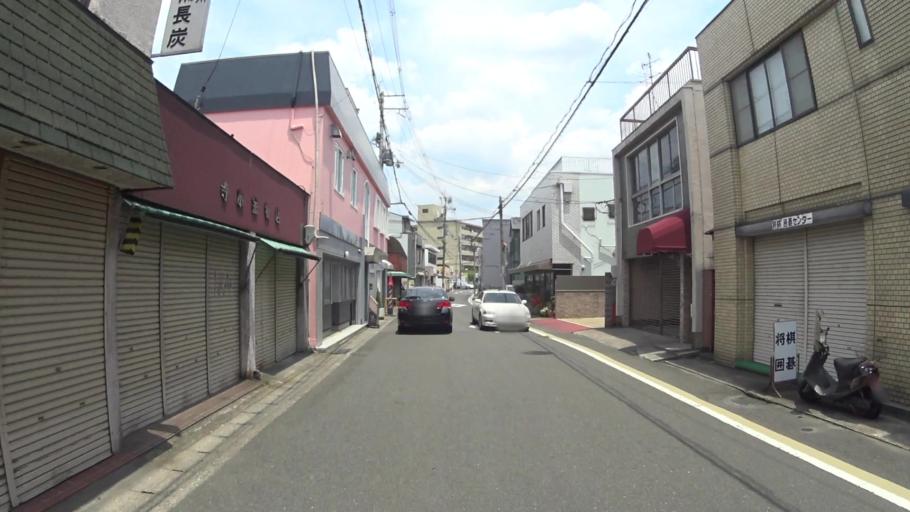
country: JP
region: Kyoto
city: Muko
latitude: 34.9790
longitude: 135.7071
